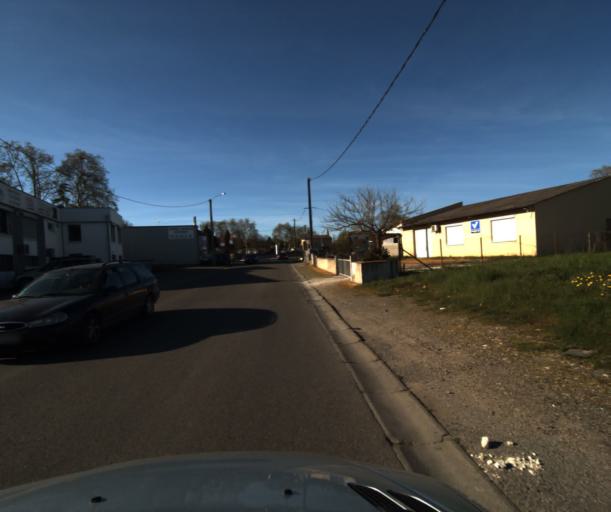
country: FR
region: Midi-Pyrenees
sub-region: Departement du Tarn-et-Garonne
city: Moissac
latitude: 44.1108
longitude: 1.1066
